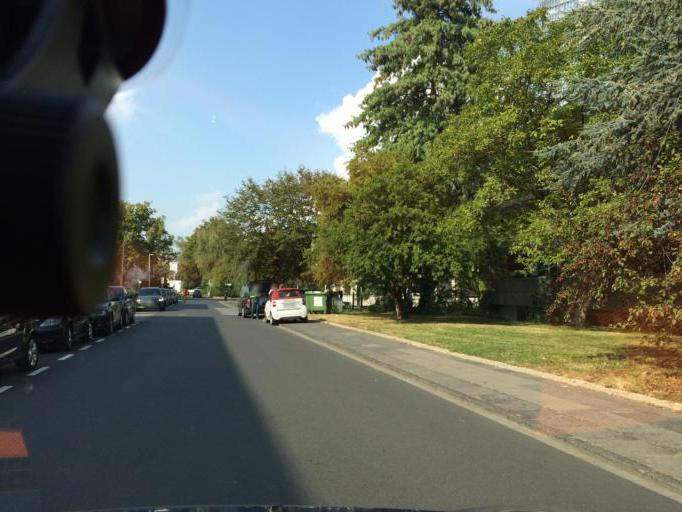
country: DE
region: North Rhine-Westphalia
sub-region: Regierungsbezirk Koln
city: Bonn
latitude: 50.7126
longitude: 7.1305
